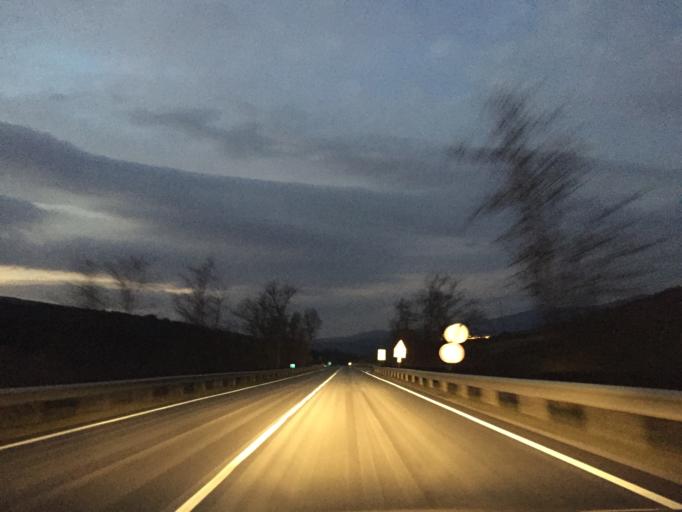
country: IT
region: Apulia
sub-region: Provincia di Foggia
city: Volturara Appula
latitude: 41.4631
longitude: 15.0583
